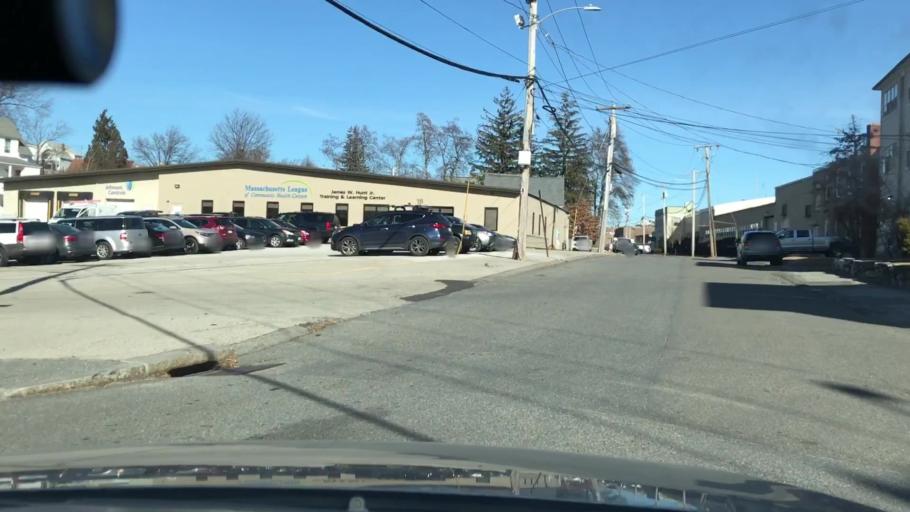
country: US
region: Massachusetts
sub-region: Worcester County
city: Worcester
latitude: 42.3095
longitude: -71.7998
